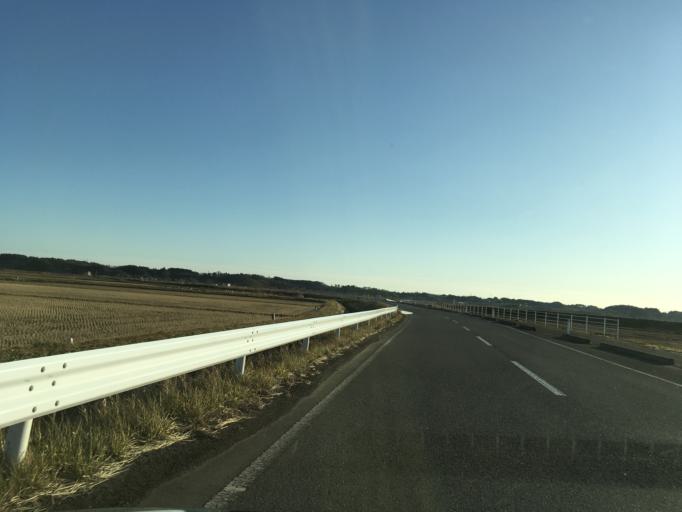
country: JP
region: Iwate
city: Ichinoseki
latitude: 38.7327
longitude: 141.1242
